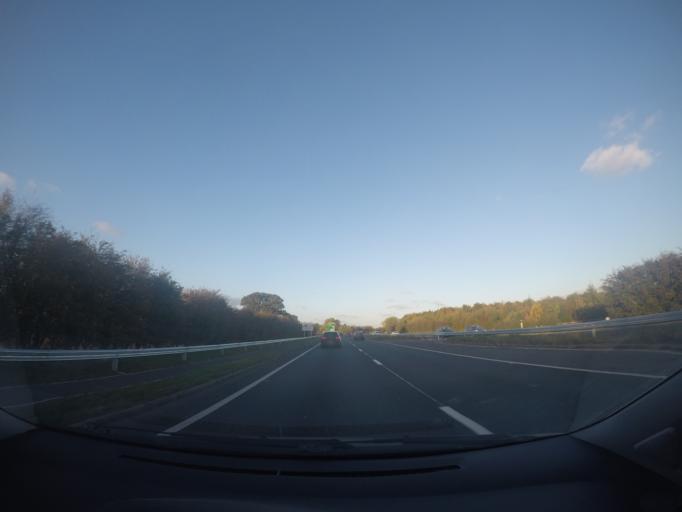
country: GB
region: England
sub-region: City of York
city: Askham Richard
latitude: 53.9120
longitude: -1.1792
